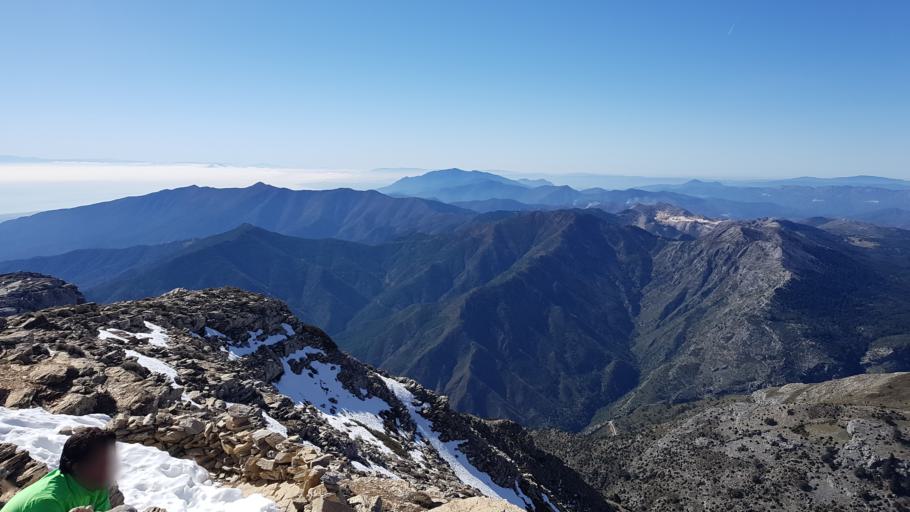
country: ES
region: Andalusia
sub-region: Provincia de Malaga
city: Tolox
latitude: 36.6760
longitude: -4.9963
